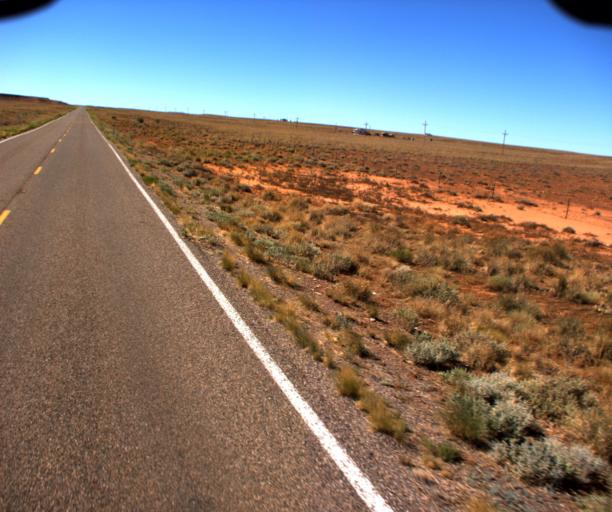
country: US
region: Arizona
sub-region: Coconino County
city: LeChee
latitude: 35.2135
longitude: -110.9508
